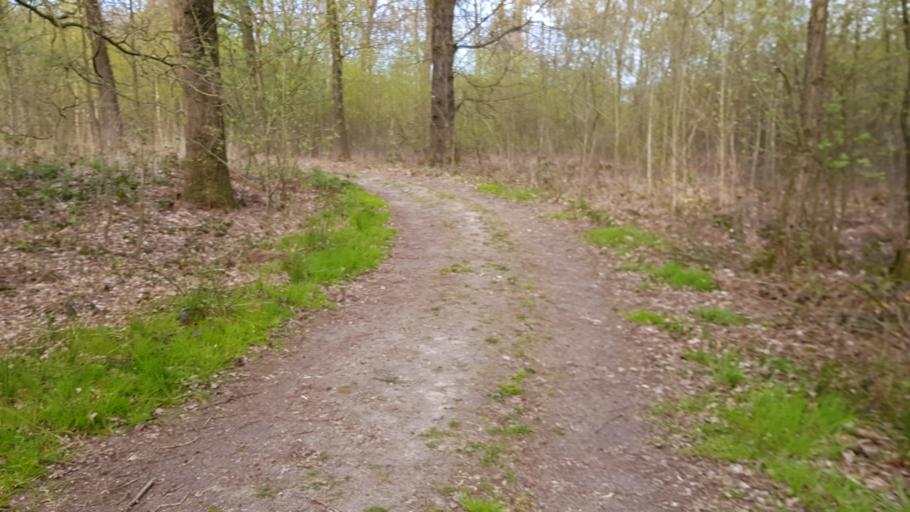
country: NL
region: Gelderland
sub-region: Gemeente Barneveld
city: Zwartebroek
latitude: 52.1906
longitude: 5.5034
